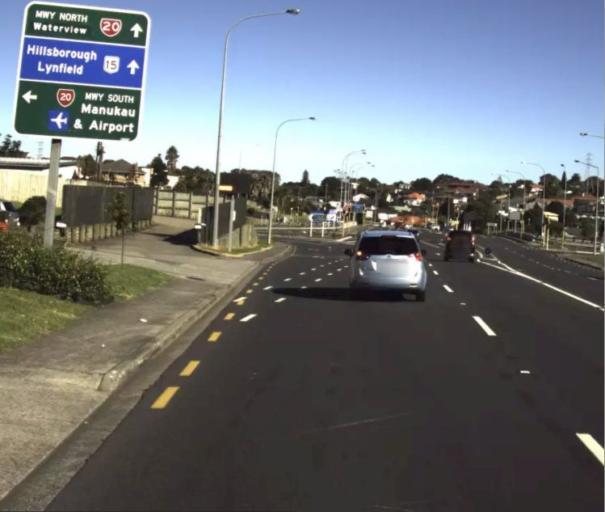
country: NZ
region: Auckland
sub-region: Auckland
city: Auckland
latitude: -36.9164
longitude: 174.7589
